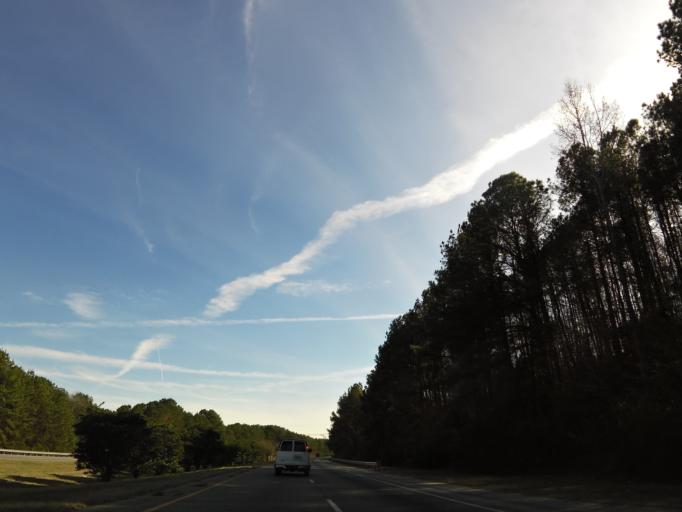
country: US
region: Alabama
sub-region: Russell County
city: Phenix City
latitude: 32.6173
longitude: -84.9515
